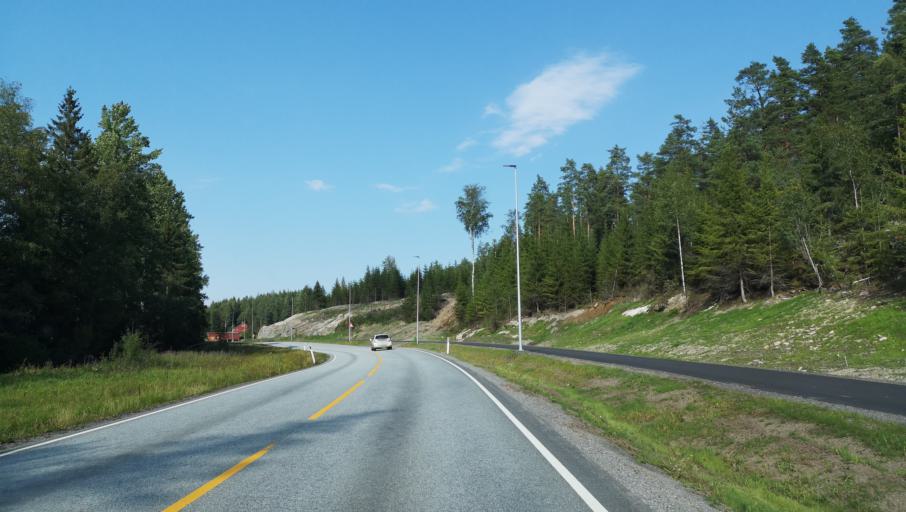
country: NO
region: Ostfold
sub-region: Valer
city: Kirkebygda
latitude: 59.4863
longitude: 10.8047
